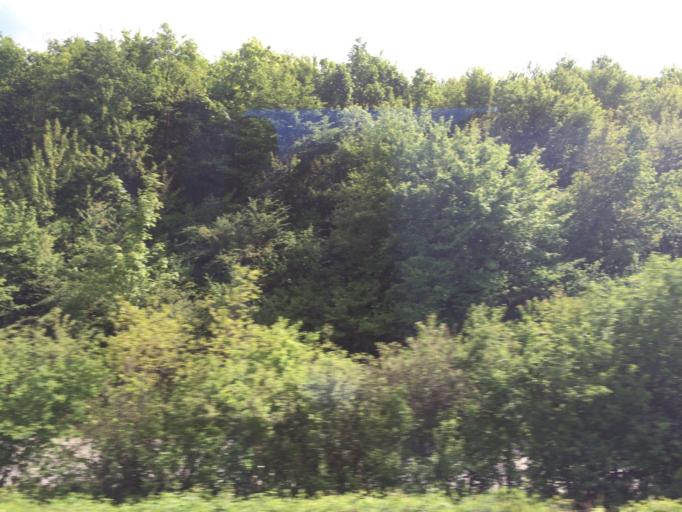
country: DE
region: Bavaria
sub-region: Regierungsbezirk Unterfranken
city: Gerbrunn
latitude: 49.7957
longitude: 9.9822
